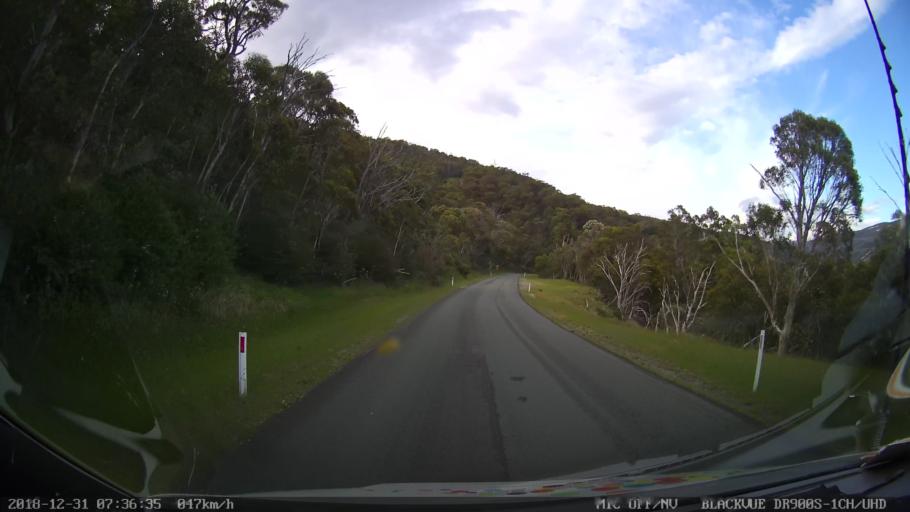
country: AU
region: New South Wales
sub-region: Snowy River
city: Jindabyne
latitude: -36.3418
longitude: 148.4420
